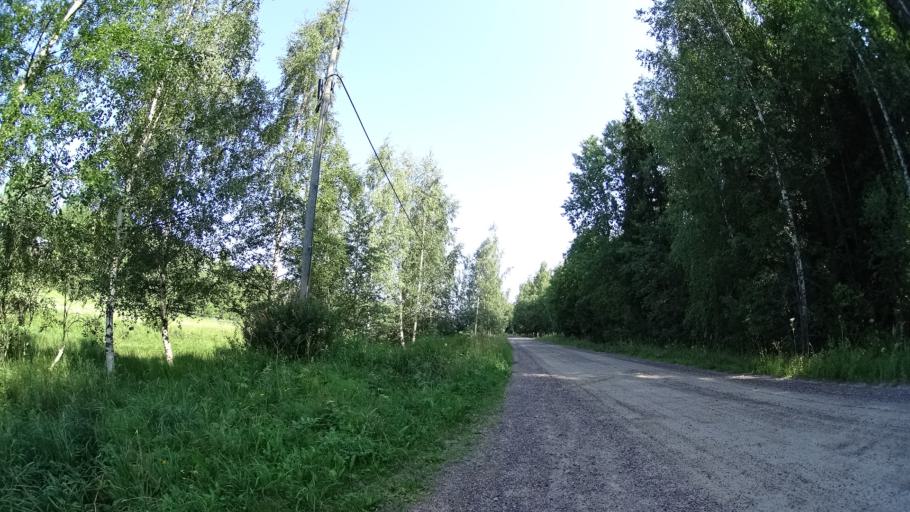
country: FI
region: Uusimaa
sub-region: Helsinki
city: Kerava
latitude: 60.3646
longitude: 25.1239
